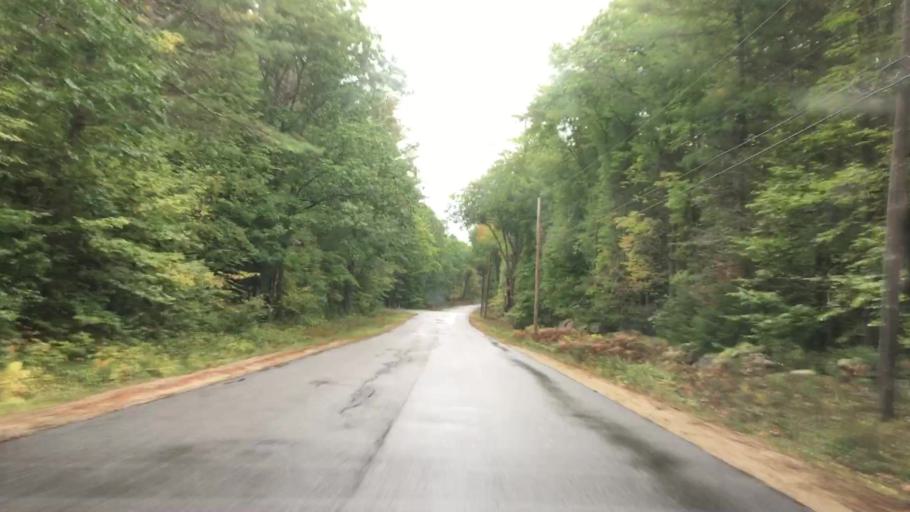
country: US
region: Maine
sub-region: Cumberland County
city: Harrison
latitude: 44.0457
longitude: -70.6136
